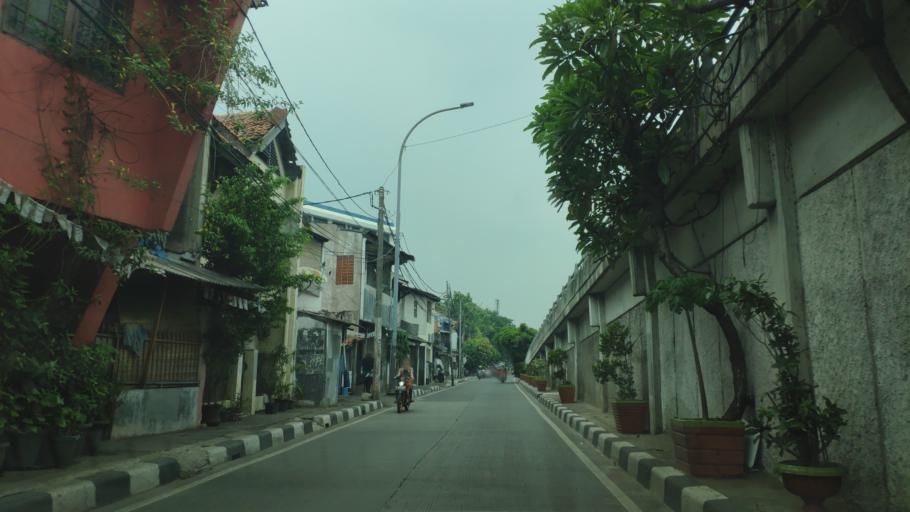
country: ID
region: Jakarta Raya
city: Jakarta
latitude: -6.1857
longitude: 106.8097
